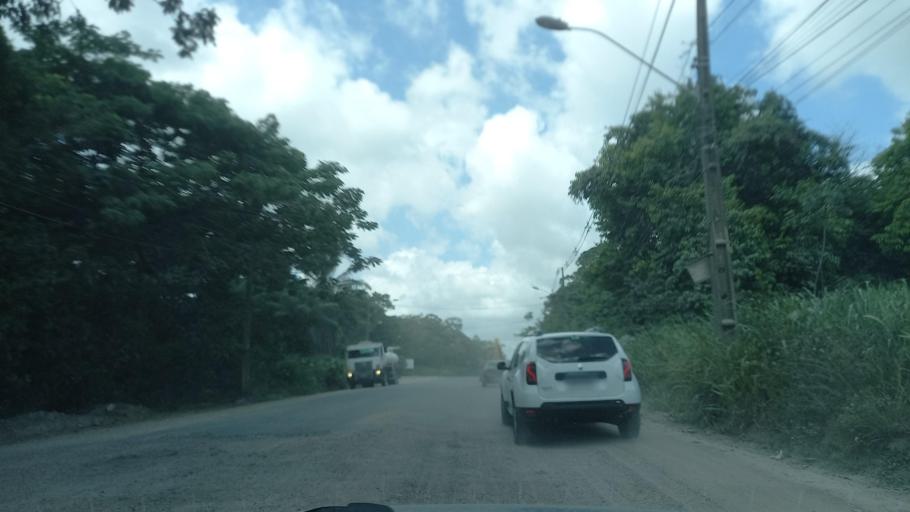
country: BR
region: Pernambuco
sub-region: Jaboatao Dos Guararapes
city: Jaboatao
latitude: -8.1595
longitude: -34.9804
